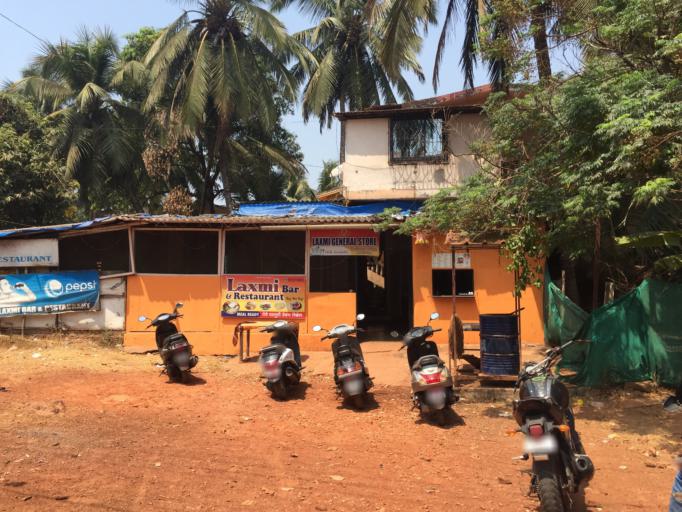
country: IN
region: Goa
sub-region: North Goa
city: Serula
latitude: 15.5469
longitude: 73.8237
